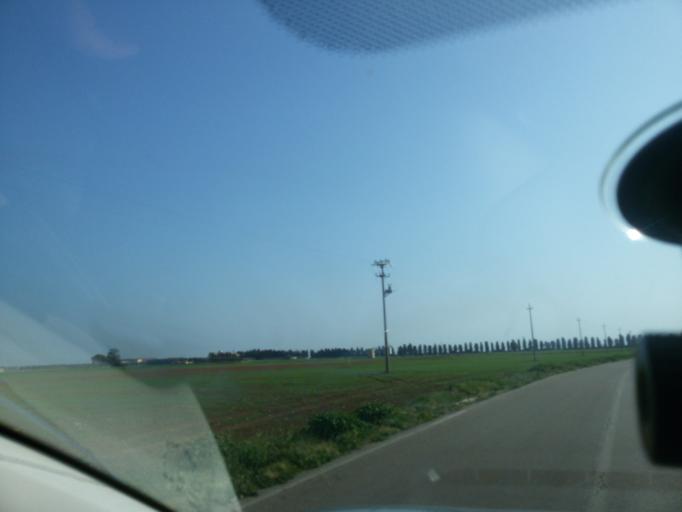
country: IT
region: Apulia
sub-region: Provincia di Brindisi
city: Mesagne
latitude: 40.6027
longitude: 17.8175
